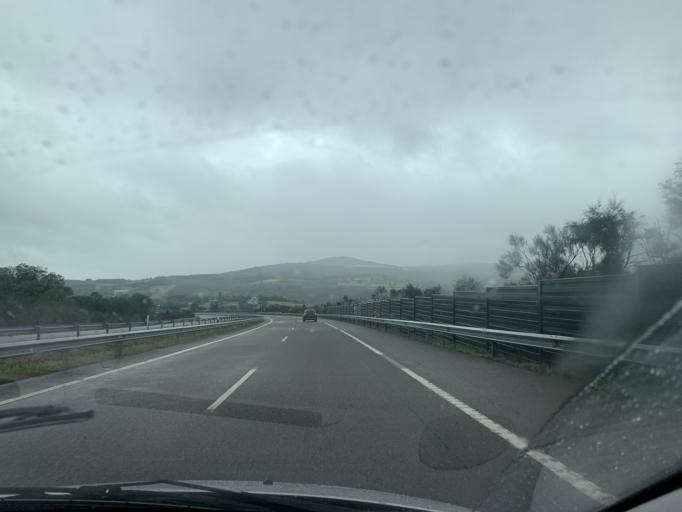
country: ES
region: Galicia
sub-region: Provincia de Lugo
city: Abadin
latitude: 43.3601
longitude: -7.4713
